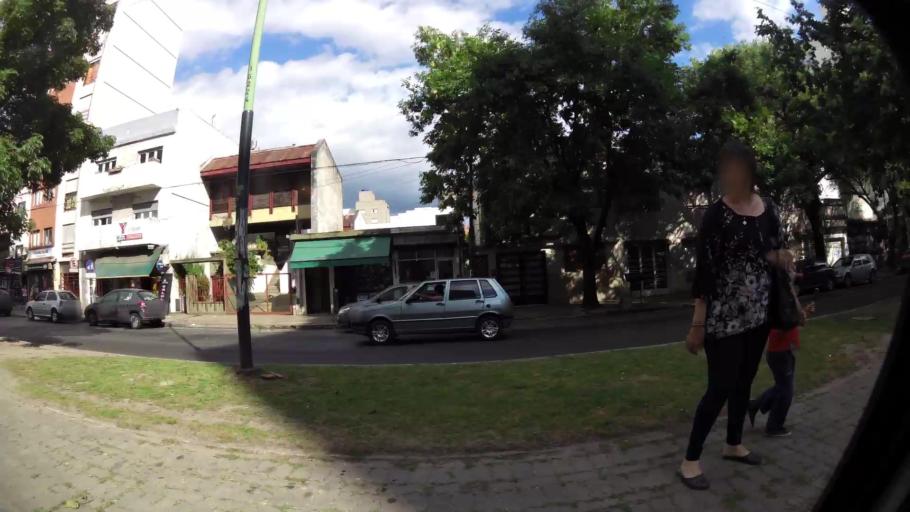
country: AR
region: Buenos Aires
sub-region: Partido de La Plata
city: La Plata
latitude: -34.9157
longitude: -57.9359
